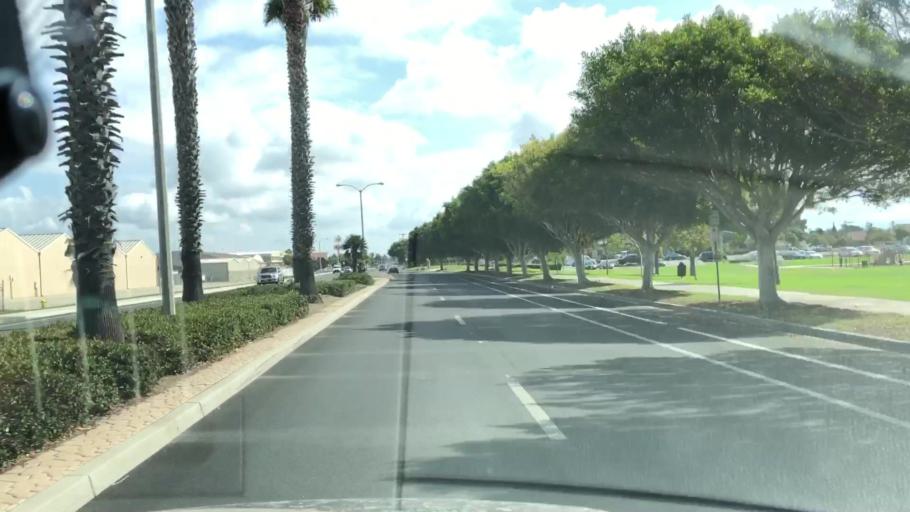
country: US
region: California
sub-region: Ventura County
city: Oxnard
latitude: 34.1974
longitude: -119.2025
